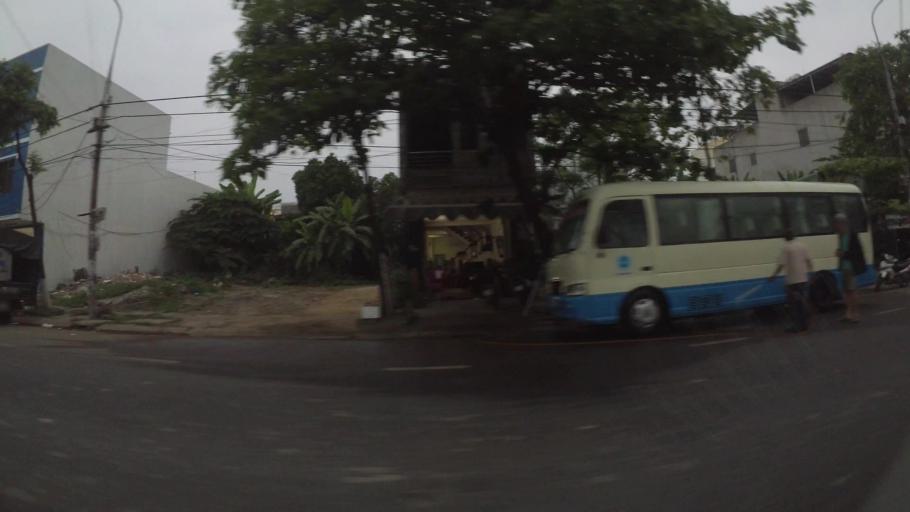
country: VN
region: Da Nang
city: Lien Chieu
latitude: 16.0546
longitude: 108.1725
